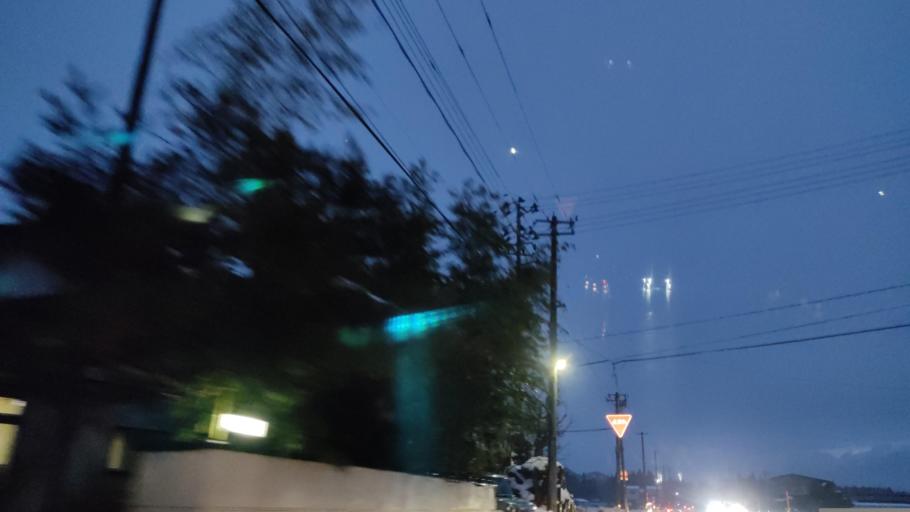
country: JP
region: Iwate
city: Morioka-shi
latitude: 39.6320
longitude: 141.1051
